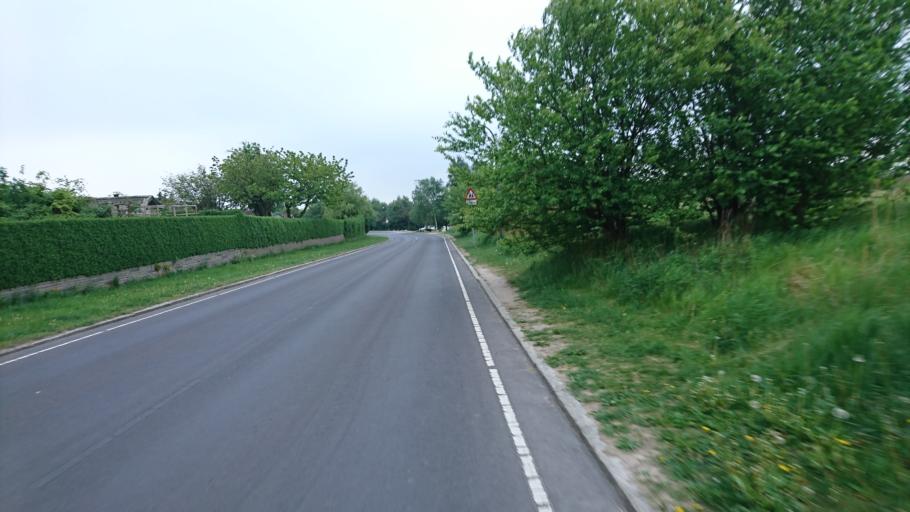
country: DK
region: Capital Region
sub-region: Herlev Kommune
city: Herlev
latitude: 55.7375
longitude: 12.4056
